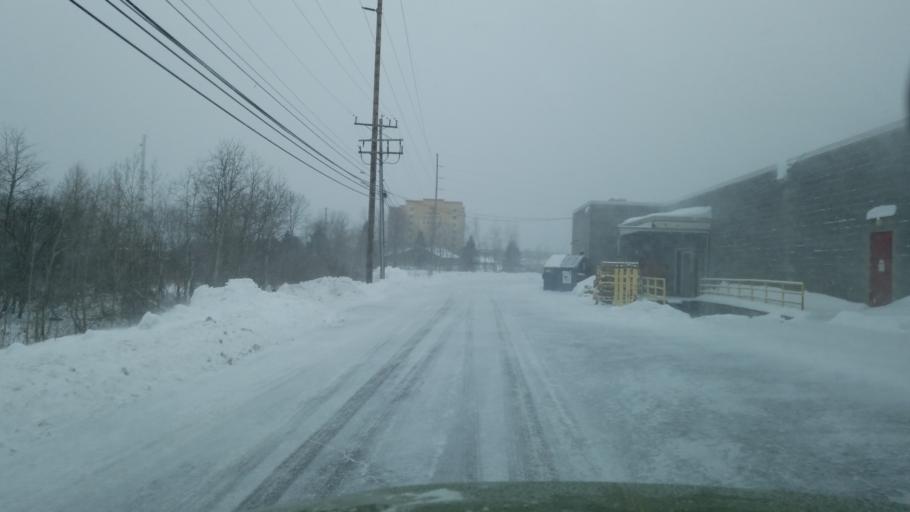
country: US
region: Pennsylvania
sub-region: Clearfield County
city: Clearfield
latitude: 41.0246
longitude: -78.4133
